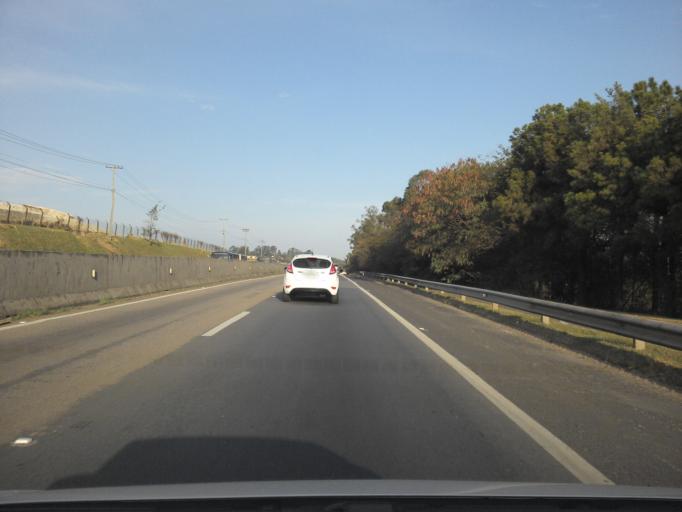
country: BR
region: Sao Paulo
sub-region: Hortolandia
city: Hortolandia
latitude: -22.8890
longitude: -47.1426
